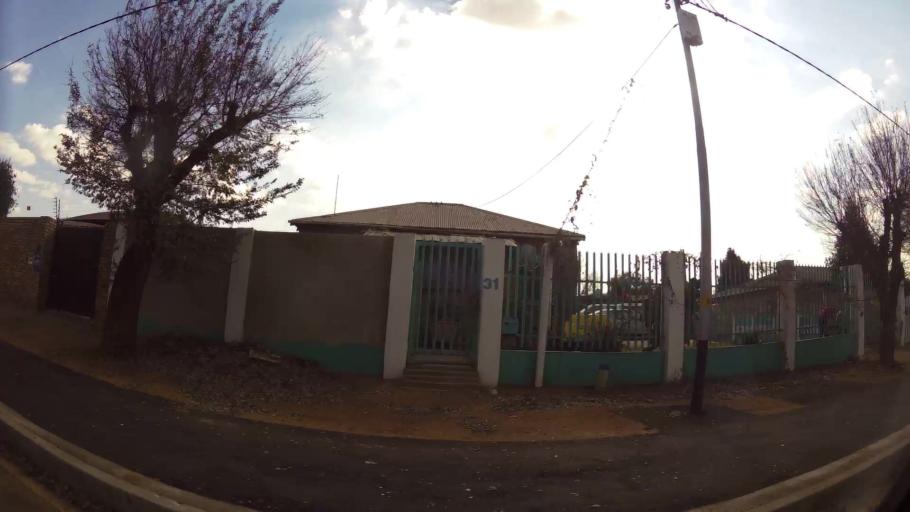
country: ZA
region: Gauteng
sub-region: Ekurhuleni Metropolitan Municipality
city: Germiston
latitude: -26.1846
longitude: 28.1769
